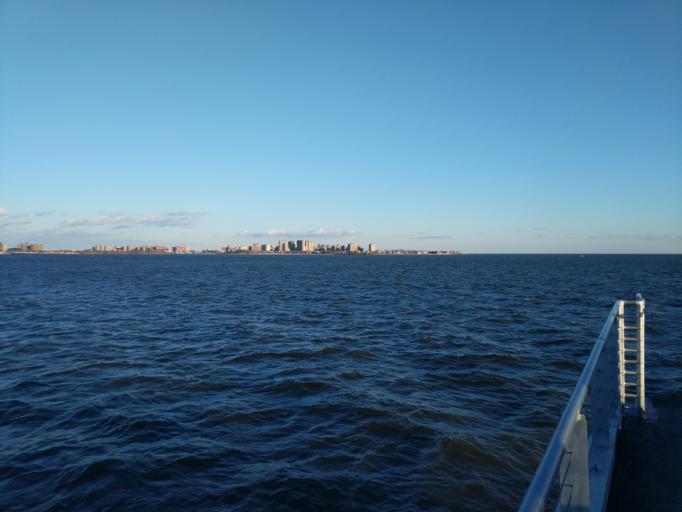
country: US
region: New York
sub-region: Kings County
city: Bensonhurst
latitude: 40.5899
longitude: -74.0274
